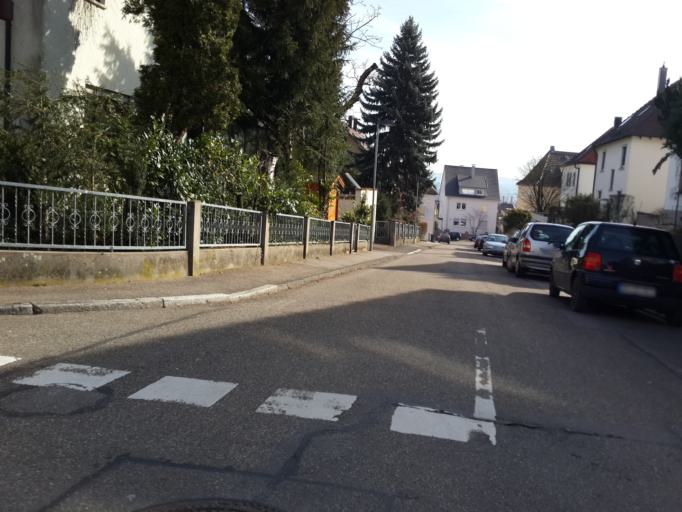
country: DE
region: Baden-Wuerttemberg
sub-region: Regierungsbezirk Stuttgart
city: Heilbronn
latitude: 49.1435
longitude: 9.1869
